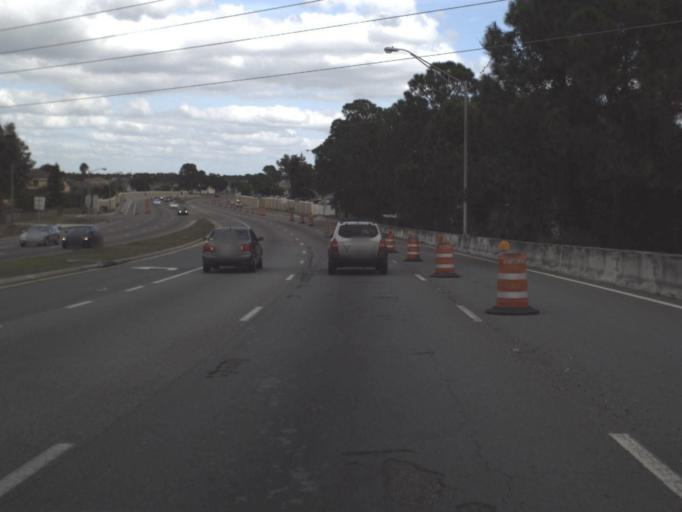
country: US
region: Florida
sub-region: Osceola County
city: Buenaventura Lakes
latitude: 28.3415
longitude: -81.3789
